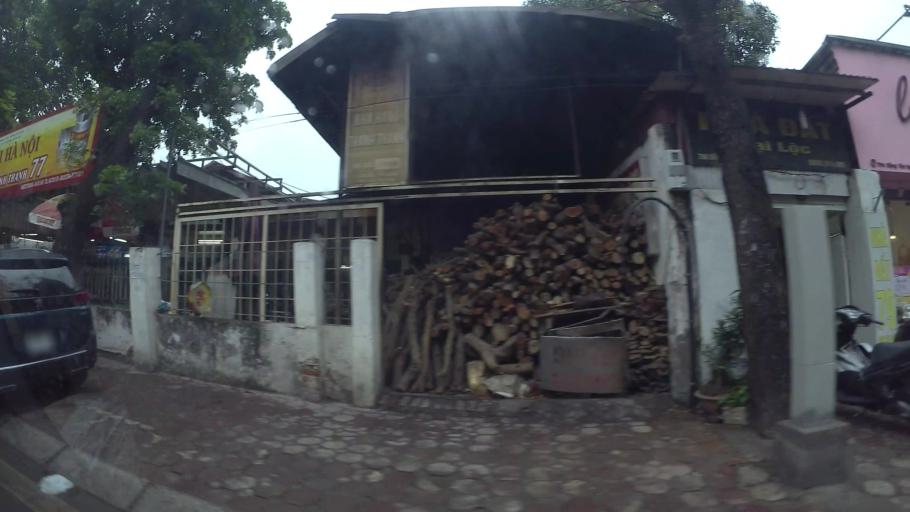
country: VN
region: Ha Noi
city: Dong Da
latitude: 21.0099
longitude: 105.8313
